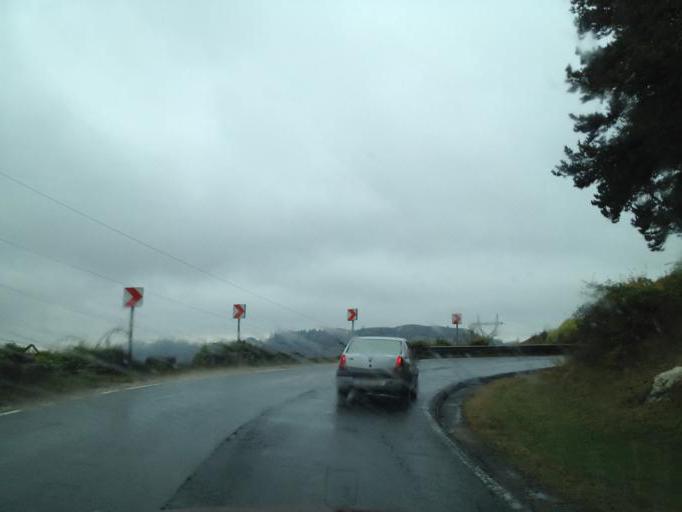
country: RO
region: Arges
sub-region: Comuna Dragoslavele
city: Dragoslavele
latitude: 45.3051
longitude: 25.1564
